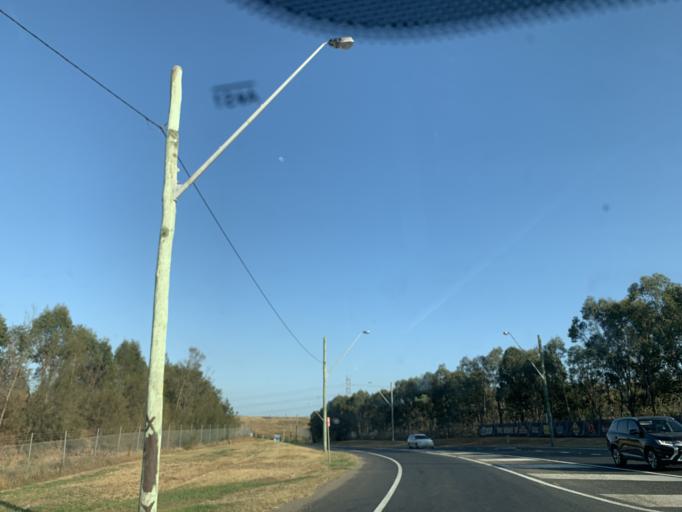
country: AU
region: New South Wales
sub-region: Fairfield
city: Horsley Park
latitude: -33.8170
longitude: 150.8676
